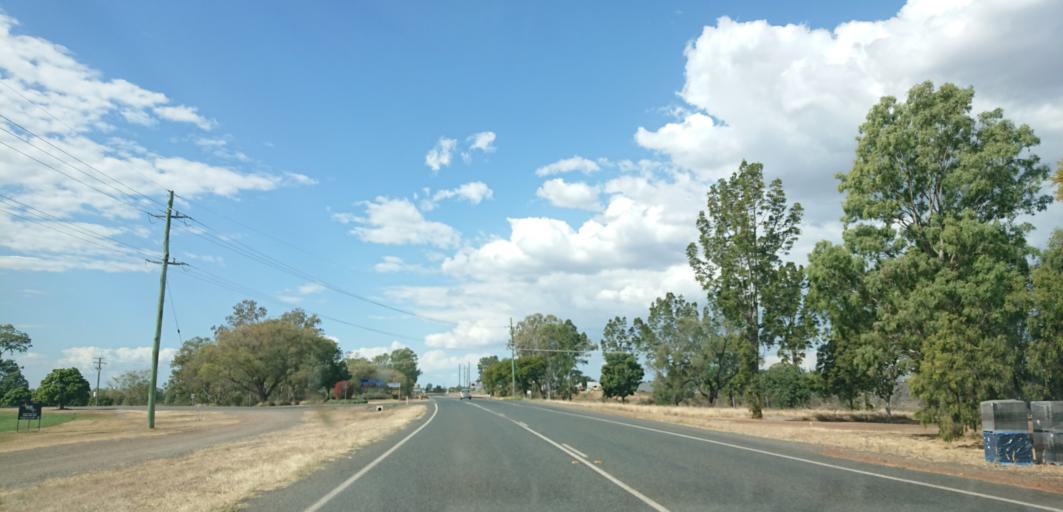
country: AU
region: Queensland
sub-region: Lockyer Valley
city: Gatton
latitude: -27.5730
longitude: 152.2544
